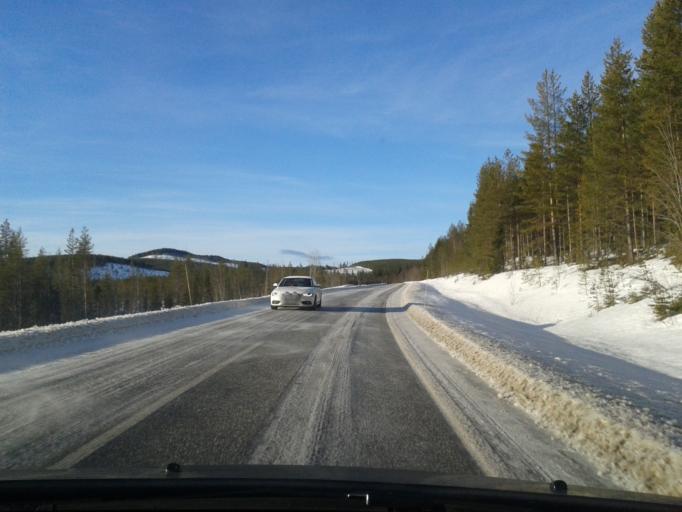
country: SE
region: Vaesternorrland
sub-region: OErnskoeldsviks Kommun
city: Bredbyn
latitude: 63.7548
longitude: 17.7052
